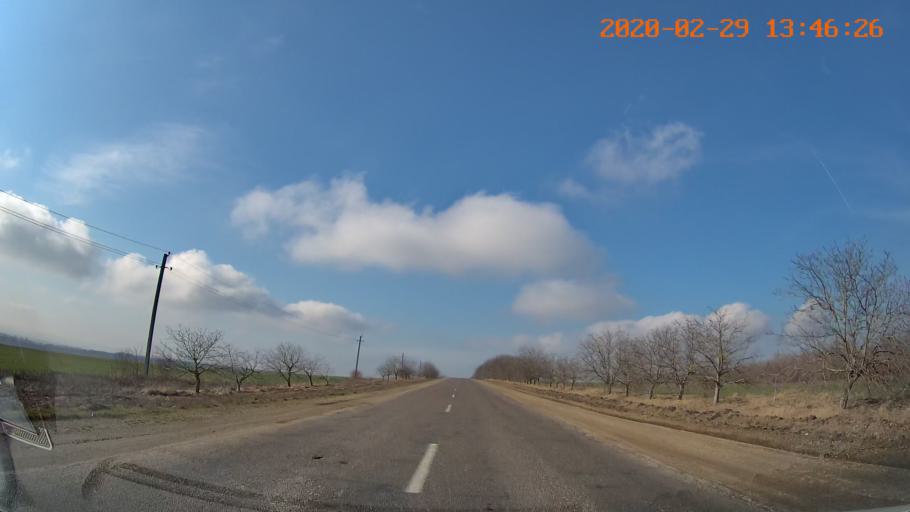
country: MD
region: Floresti
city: Leninskiy
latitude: 47.8565
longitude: 28.5055
